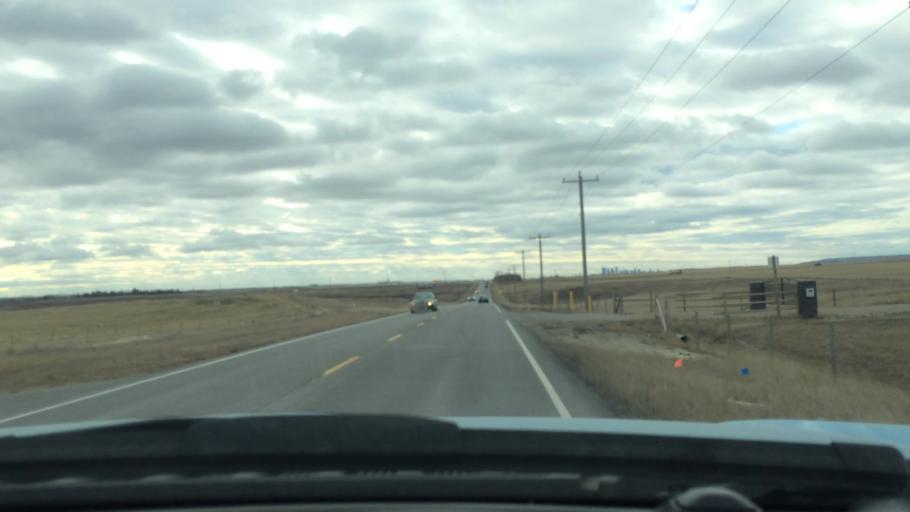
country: CA
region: Alberta
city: Airdrie
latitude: 51.2191
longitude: -114.0250
